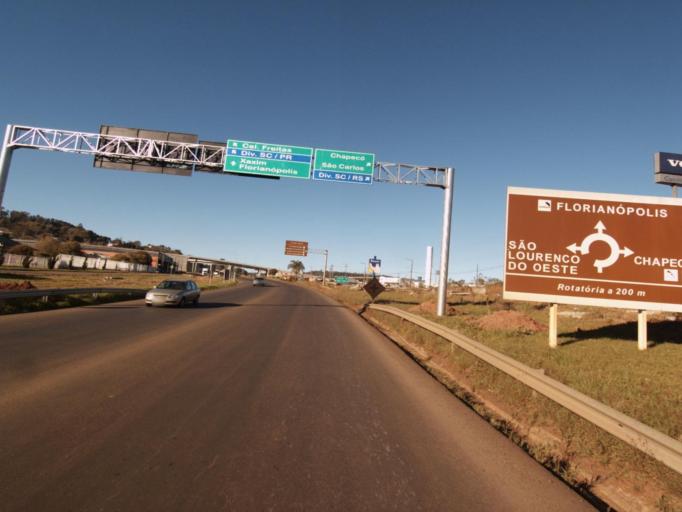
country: BR
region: Santa Catarina
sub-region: Chapeco
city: Chapeco
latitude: -27.0007
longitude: -52.6494
